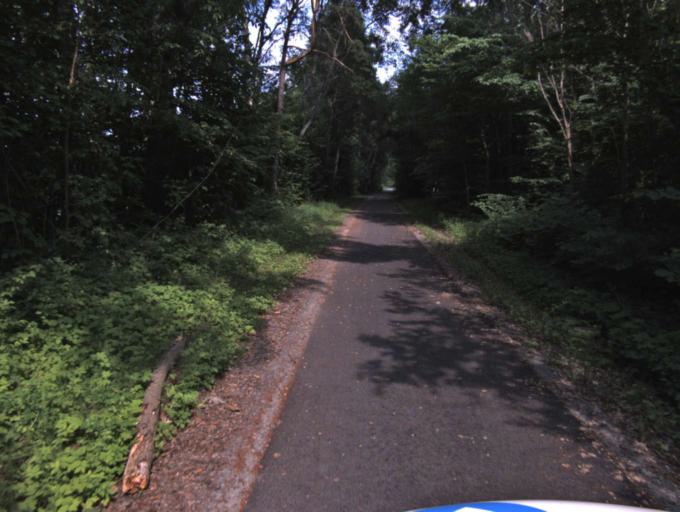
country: SE
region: Skane
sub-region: Kristianstads Kommun
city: Fjalkinge
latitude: 56.0828
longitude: 14.2259
